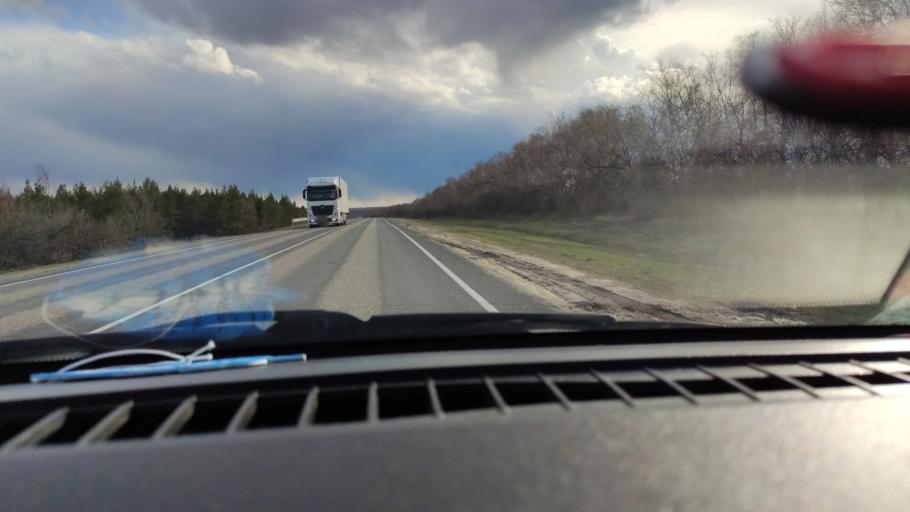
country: RU
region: Saratov
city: Sinodskoye
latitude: 51.9384
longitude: 46.5939
